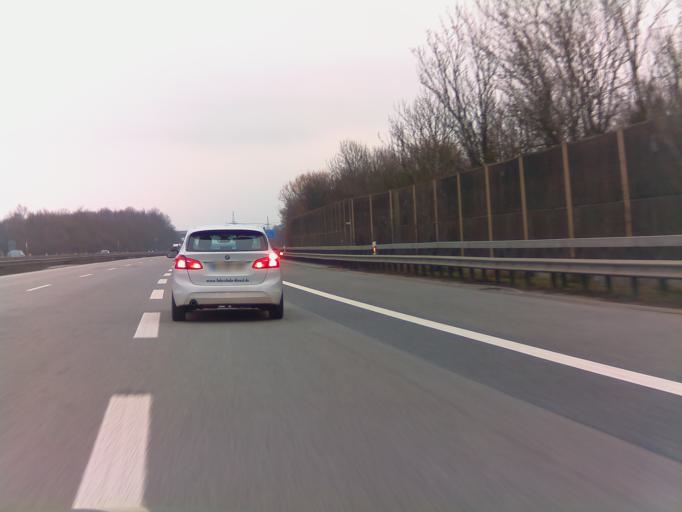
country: DE
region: Rheinland-Pfalz
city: Albig
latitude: 49.7674
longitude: 8.1127
